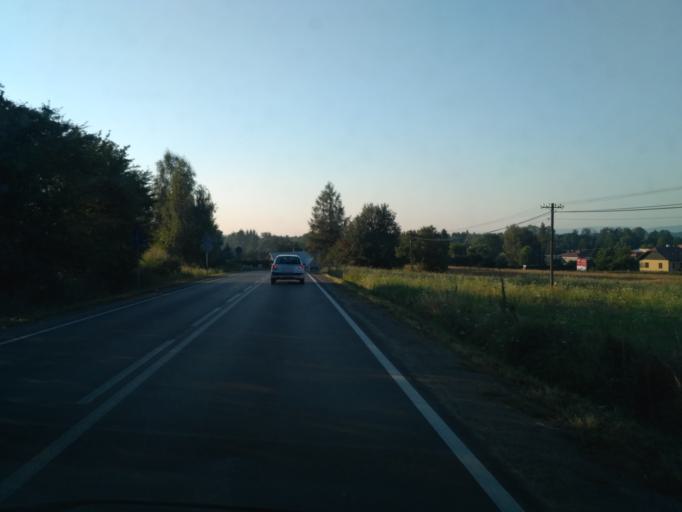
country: PL
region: Subcarpathian Voivodeship
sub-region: Powiat krosnienski
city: Korczyna
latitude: 49.7218
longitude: 21.8108
